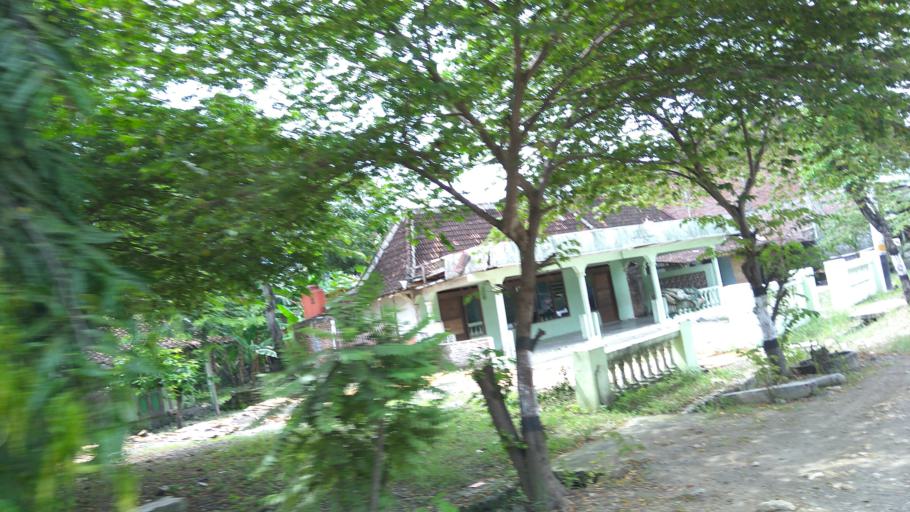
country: ID
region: Central Java
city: Mranggen
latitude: -7.0640
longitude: 110.6660
